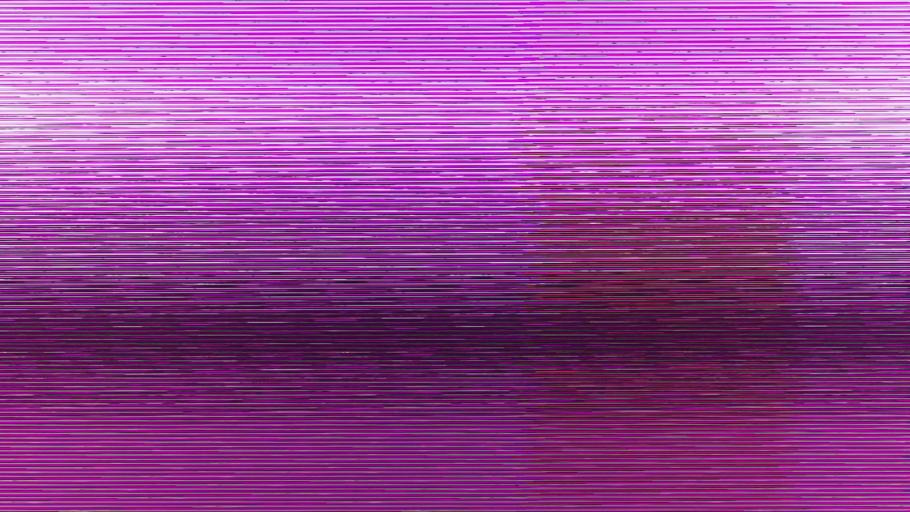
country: US
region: Michigan
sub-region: Genesee County
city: Flushing
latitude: 43.0395
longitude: -83.7738
